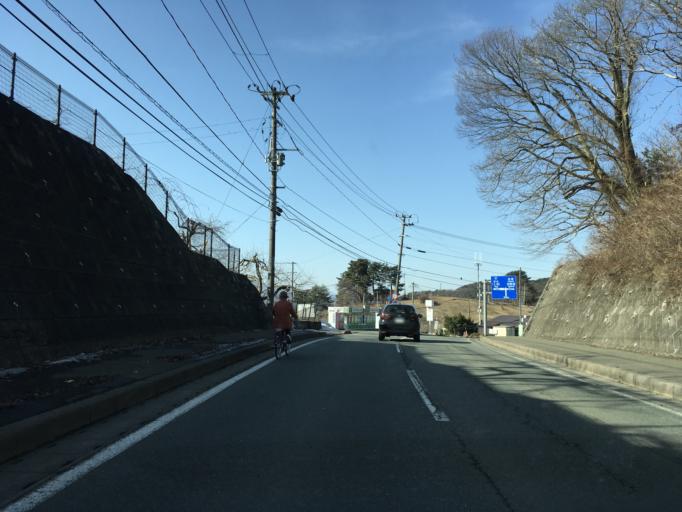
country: JP
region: Iwate
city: Morioka-shi
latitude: 39.7236
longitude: 141.1571
